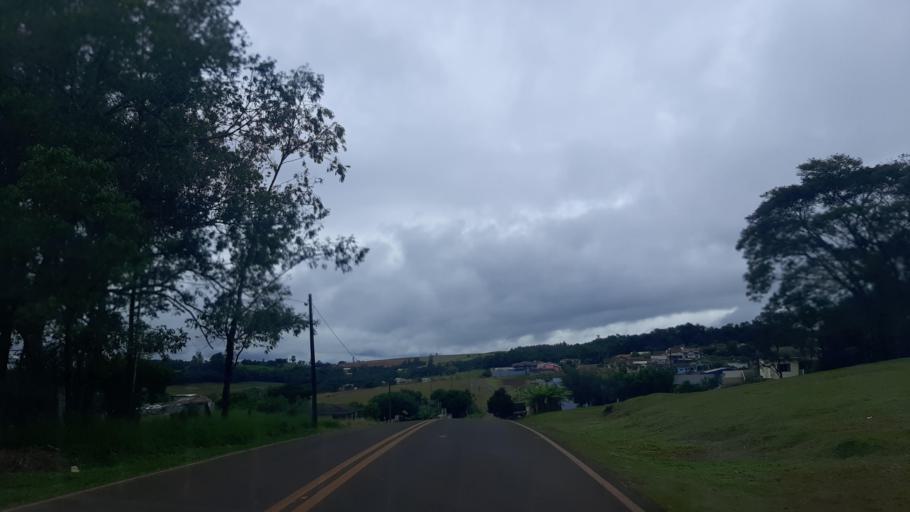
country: BR
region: Parana
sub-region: Ampere
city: Ampere
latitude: -25.9270
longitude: -53.4671
